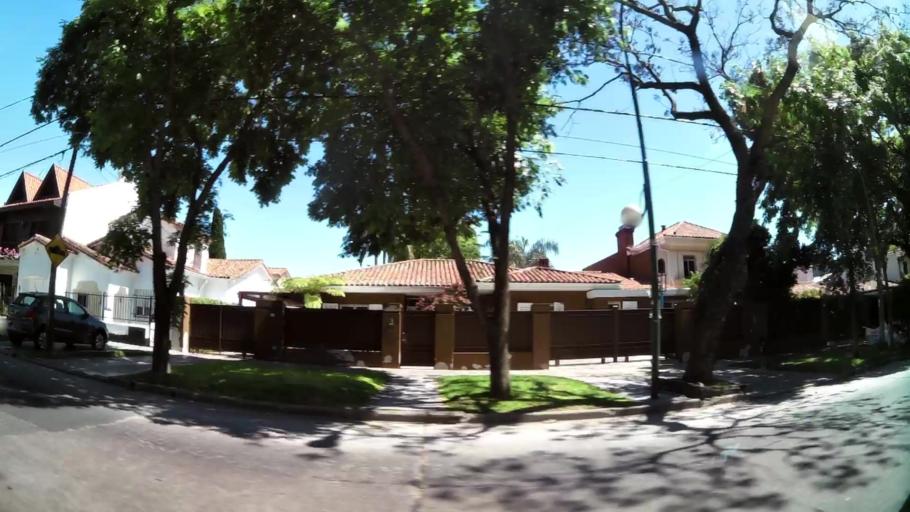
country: AR
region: Buenos Aires
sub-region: Partido de Vicente Lopez
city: Olivos
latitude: -34.4960
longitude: -58.4939
